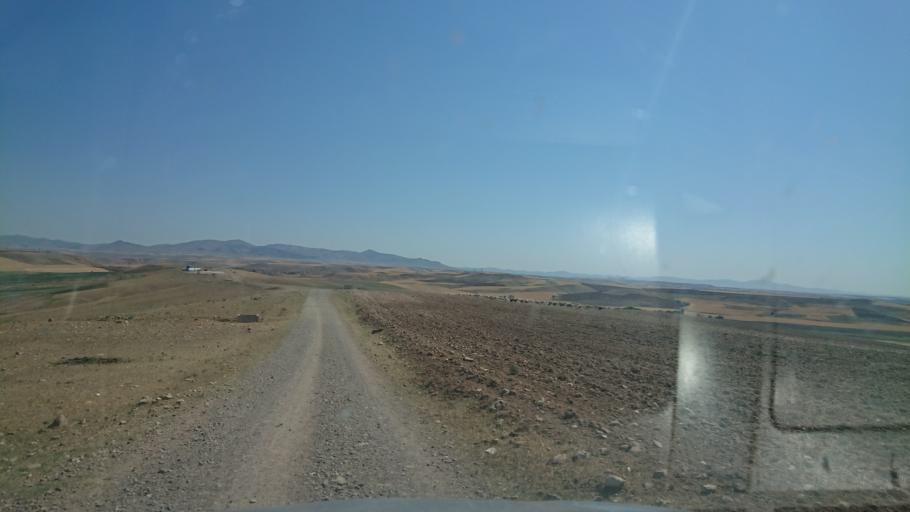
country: TR
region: Aksaray
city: Sariyahsi
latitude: 39.0552
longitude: 33.8873
